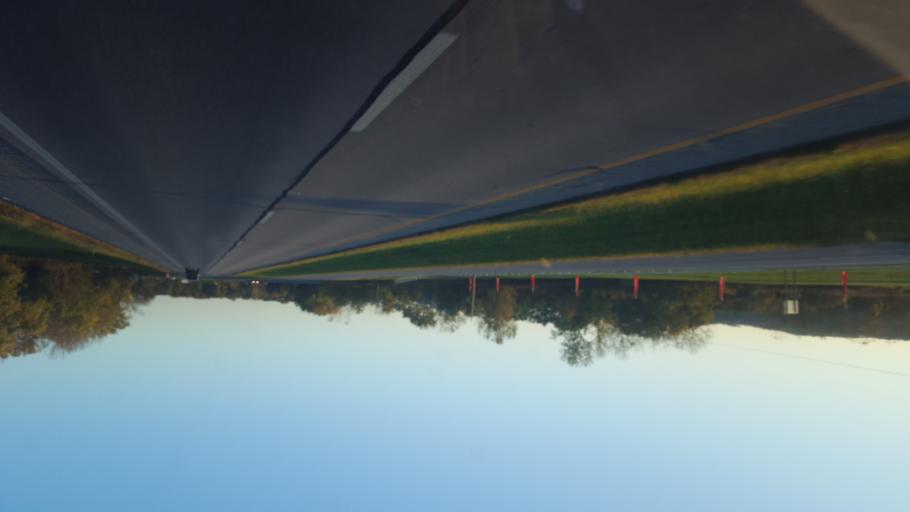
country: US
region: Ohio
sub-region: Pike County
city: Piketon
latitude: 38.9783
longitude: -83.0227
